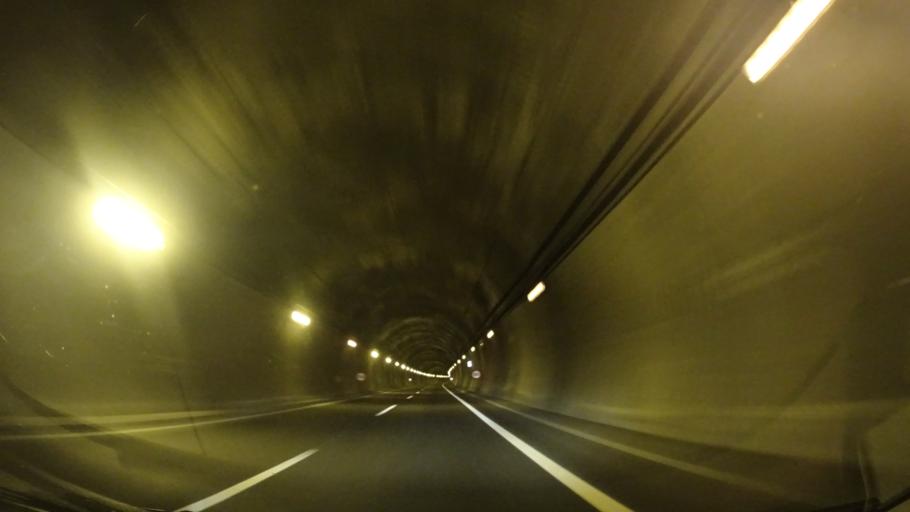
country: ES
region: Castille and Leon
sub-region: Provincia de Leon
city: Soto y Amio
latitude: 42.8546
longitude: -5.8732
